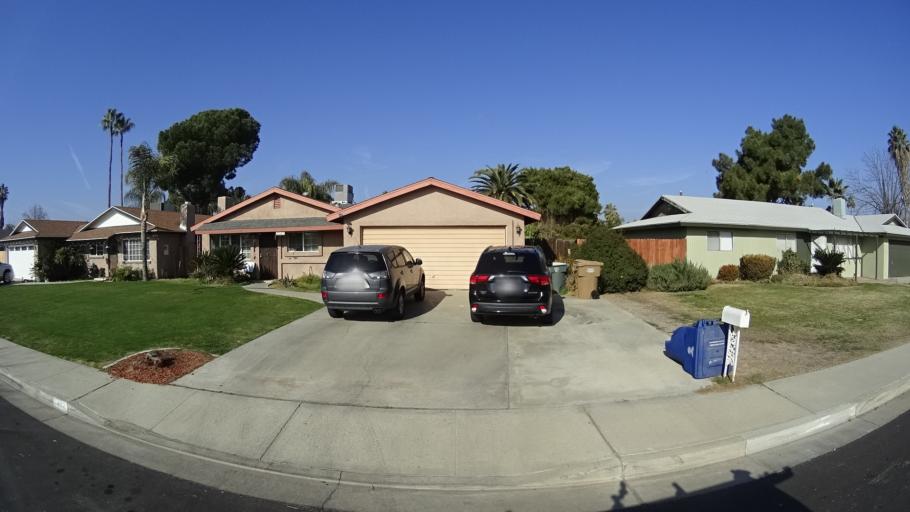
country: US
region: California
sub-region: Kern County
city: Bakersfield
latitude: 35.3291
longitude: -119.0596
